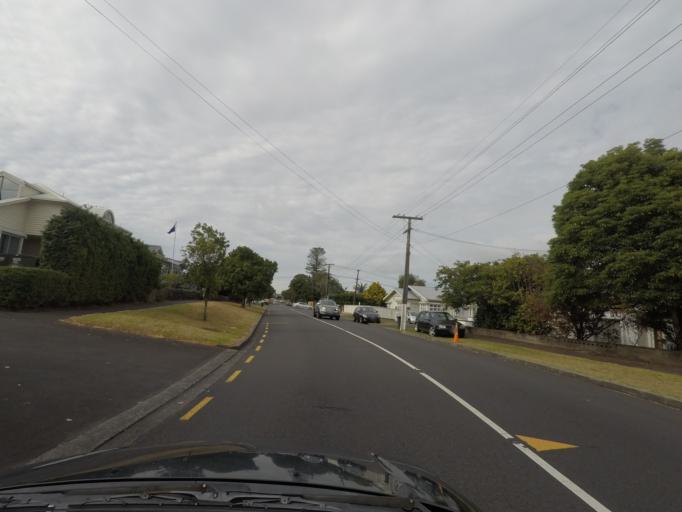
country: NZ
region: Auckland
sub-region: Auckland
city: Rosebank
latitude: -36.8861
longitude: 174.7099
